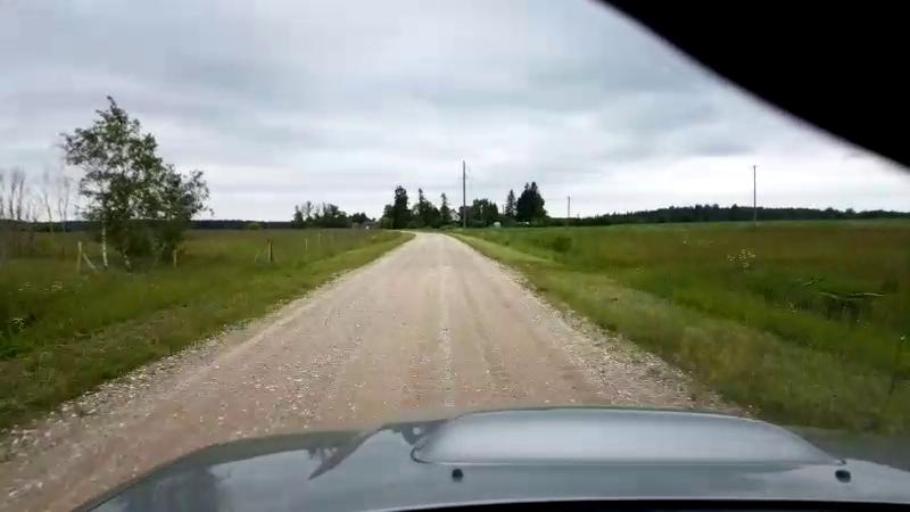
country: EE
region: Paernumaa
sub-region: Halinga vald
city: Parnu-Jaagupi
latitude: 58.5415
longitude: 24.5587
